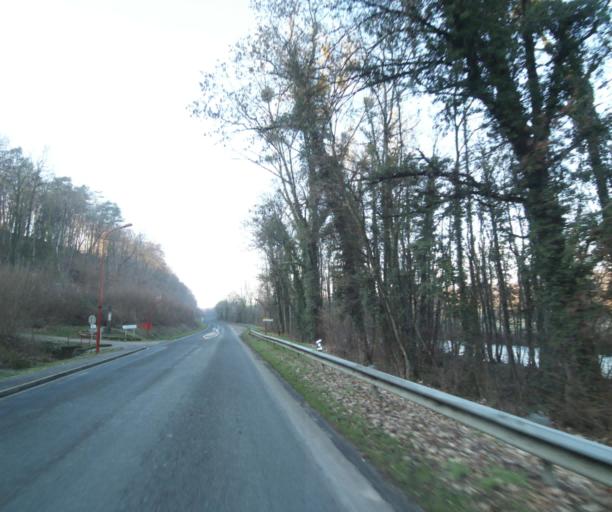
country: FR
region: Champagne-Ardenne
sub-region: Departement de la Haute-Marne
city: Bienville
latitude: 48.5508
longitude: 5.0704
